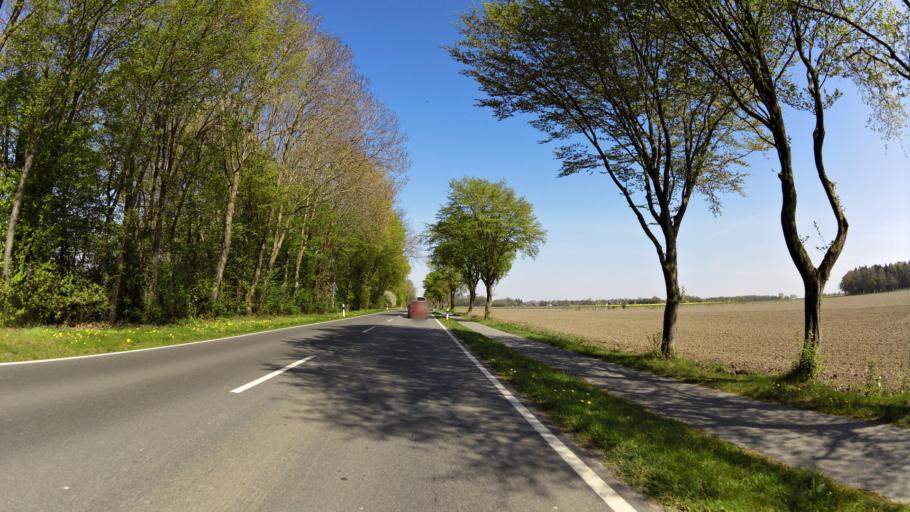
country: DE
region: Lower Saxony
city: Ganderkesee
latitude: 53.0760
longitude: 8.5260
